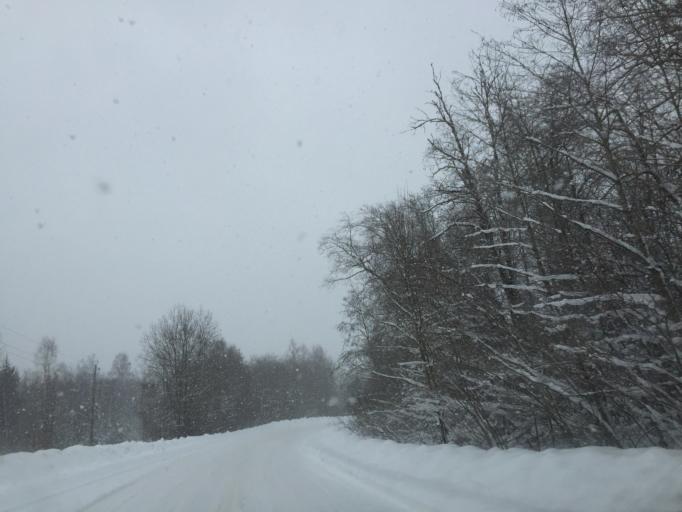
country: LV
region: Amatas Novads
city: Drabesi
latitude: 57.0828
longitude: 25.3467
